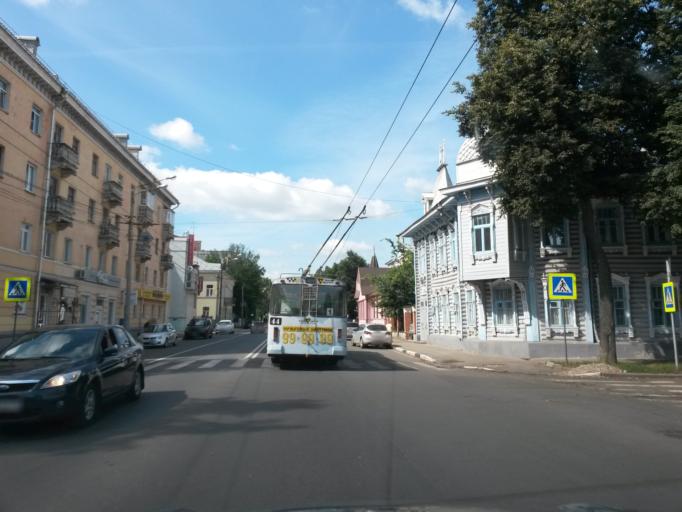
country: RU
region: Jaroslavl
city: Yaroslavl
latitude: 57.6342
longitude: 39.8841
